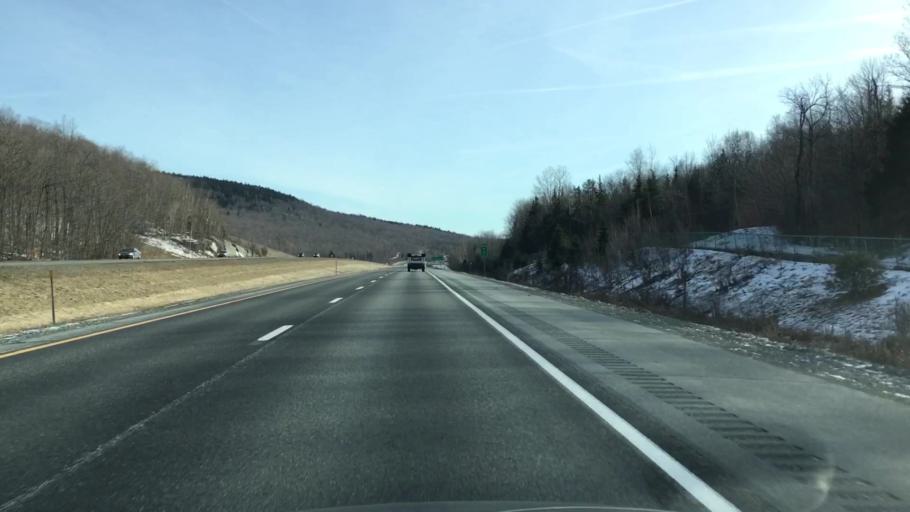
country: US
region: New Hampshire
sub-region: Grafton County
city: Enfield
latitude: 43.5715
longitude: -72.1565
